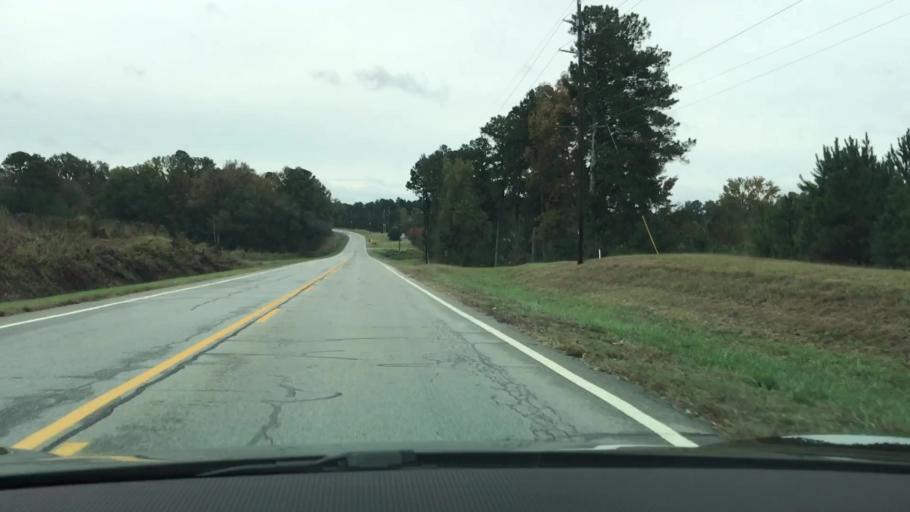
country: US
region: Georgia
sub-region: Warren County
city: Warrenton
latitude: 33.3970
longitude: -82.6529
